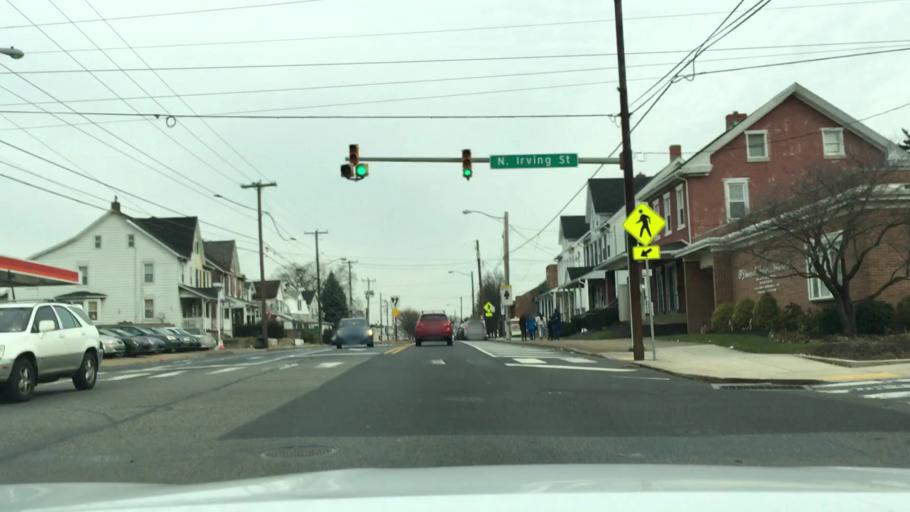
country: US
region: Pennsylvania
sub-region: Lehigh County
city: Fullerton
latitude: 40.6169
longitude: -75.4418
